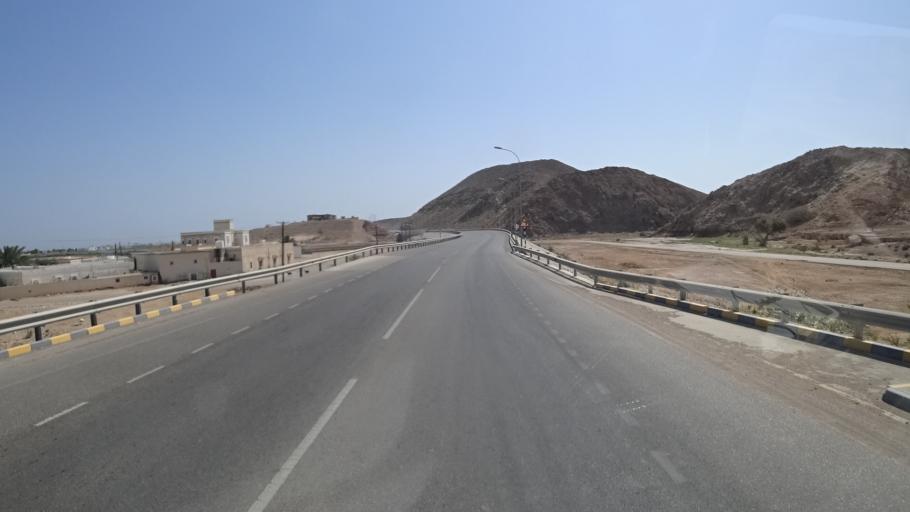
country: OM
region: Ash Sharqiyah
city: Sur
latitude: 22.5488
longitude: 59.5250
